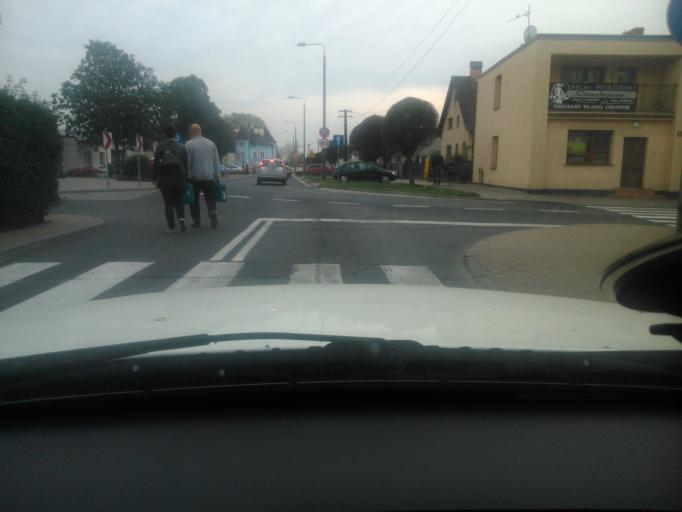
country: PL
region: Kujawsko-Pomorskie
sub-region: Powiat golubsko-dobrzynski
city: Kowalewo Pomorskie
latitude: 53.1533
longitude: 18.8973
